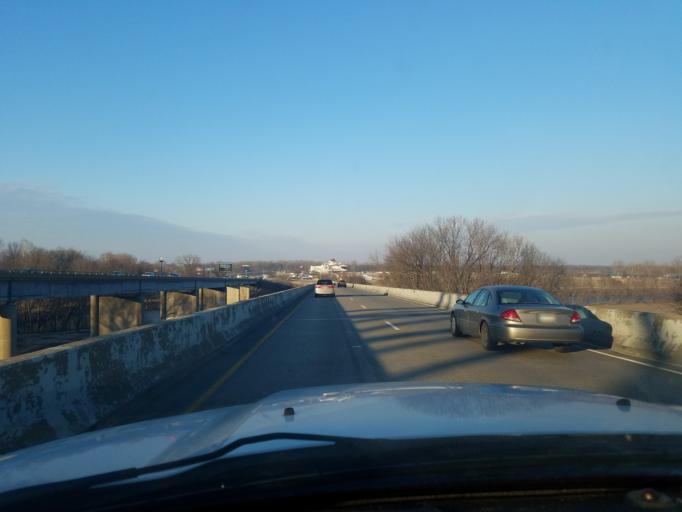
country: US
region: Indiana
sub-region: Vanderburgh County
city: Evansville
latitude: 37.9089
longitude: -87.5492
